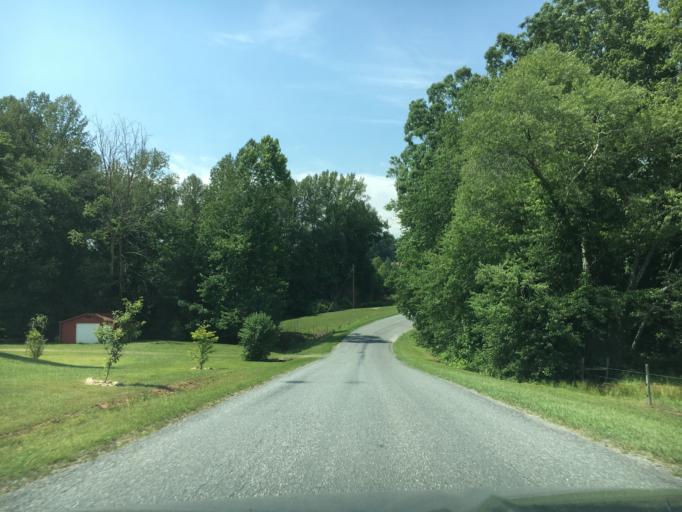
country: US
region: Virginia
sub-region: Pittsylvania County
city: Gretna
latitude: 36.9471
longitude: -79.4422
